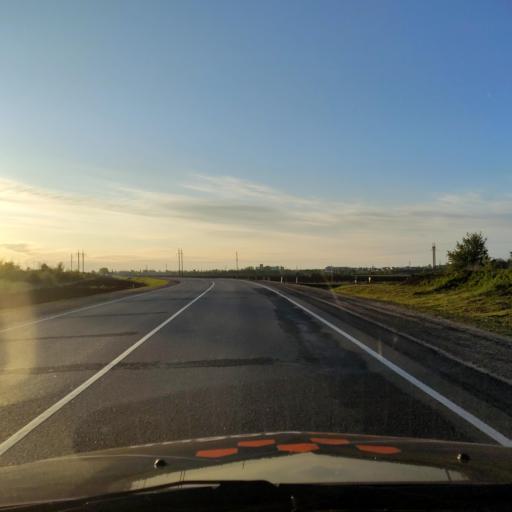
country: RU
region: Orjol
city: Livny
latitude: 52.4408
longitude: 37.5526
